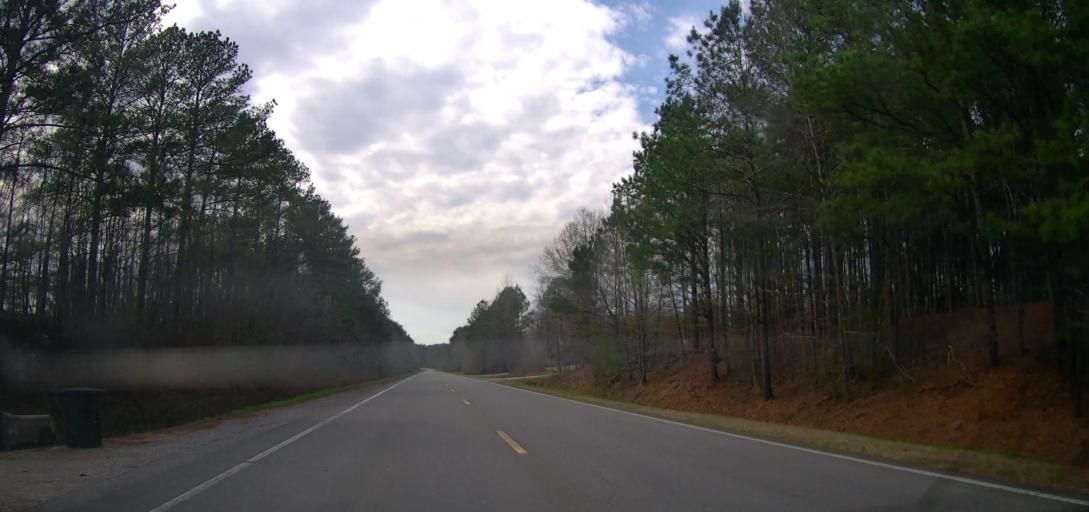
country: US
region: Alabama
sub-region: Marion County
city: Winfield
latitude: 33.9347
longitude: -87.7154
